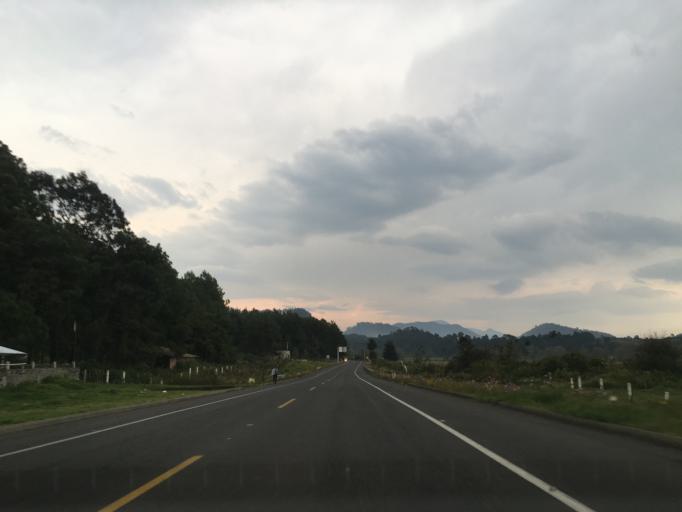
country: MX
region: Michoacan
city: Capacuaro
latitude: 19.5062
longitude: -102.1265
